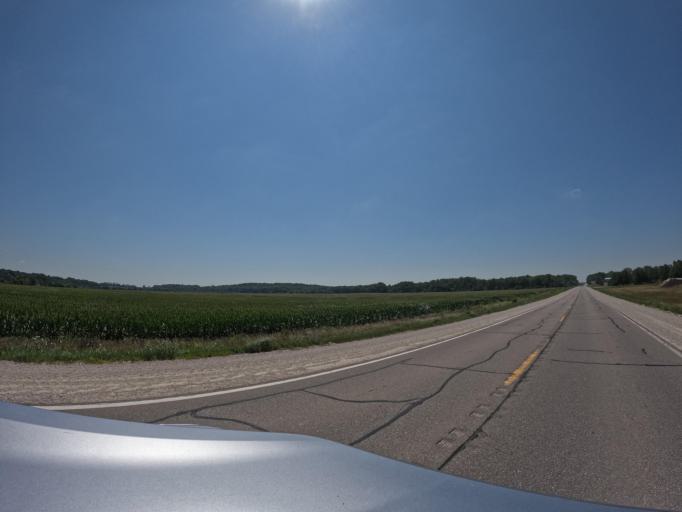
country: US
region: Iowa
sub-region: Keokuk County
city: Sigourney
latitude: 41.3144
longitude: -92.2051
